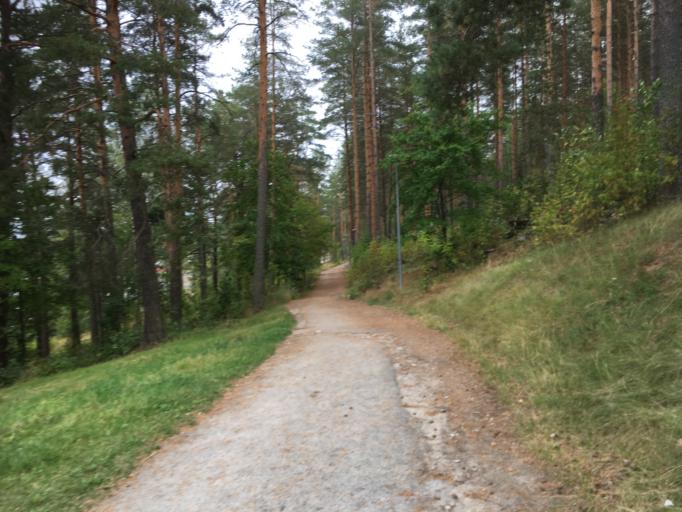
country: FI
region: Central Finland
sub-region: Jyvaeskylae
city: Jyvaeskylae
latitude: 62.2410
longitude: 25.7358
